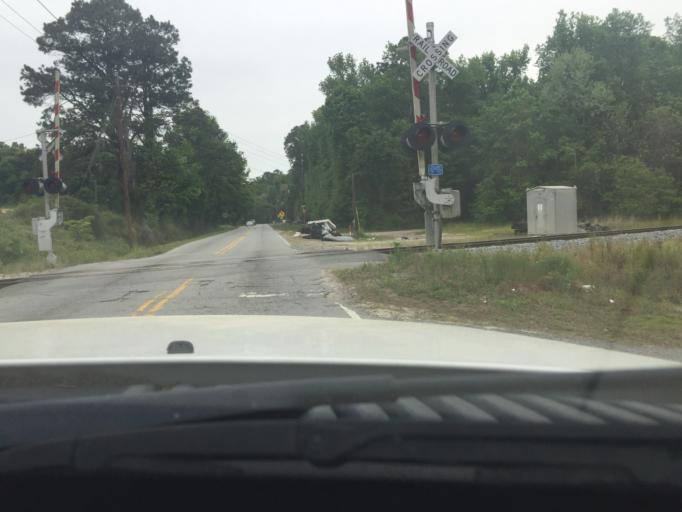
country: US
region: Georgia
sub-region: Chatham County
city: Georgetown
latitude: 31.9759
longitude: -81.2481
